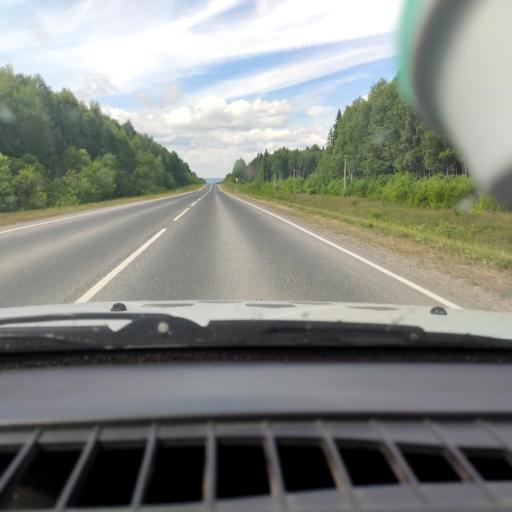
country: RU
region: Perm
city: Verkhnechusovskiye Gorodki
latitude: 58.2669
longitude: 56.9592
